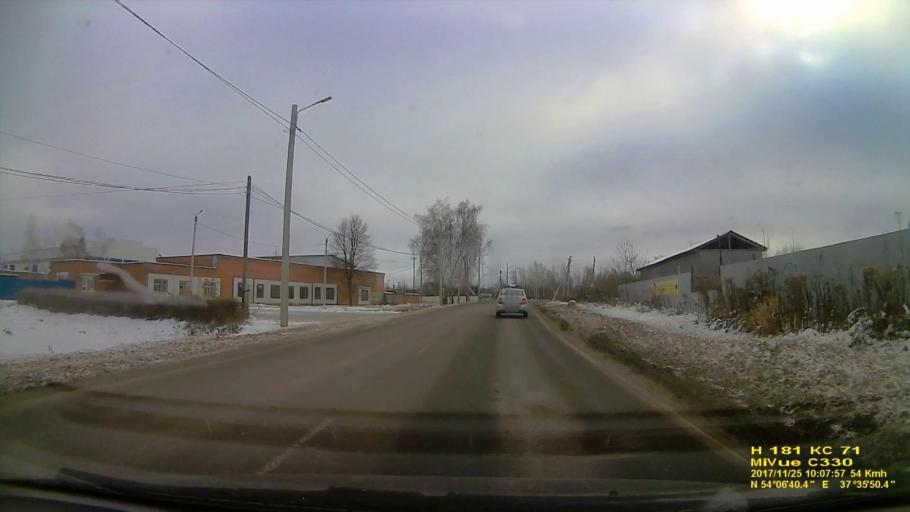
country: RU
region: Tula
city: Skuratovskiy
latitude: 54.1111
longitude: 37.5978
